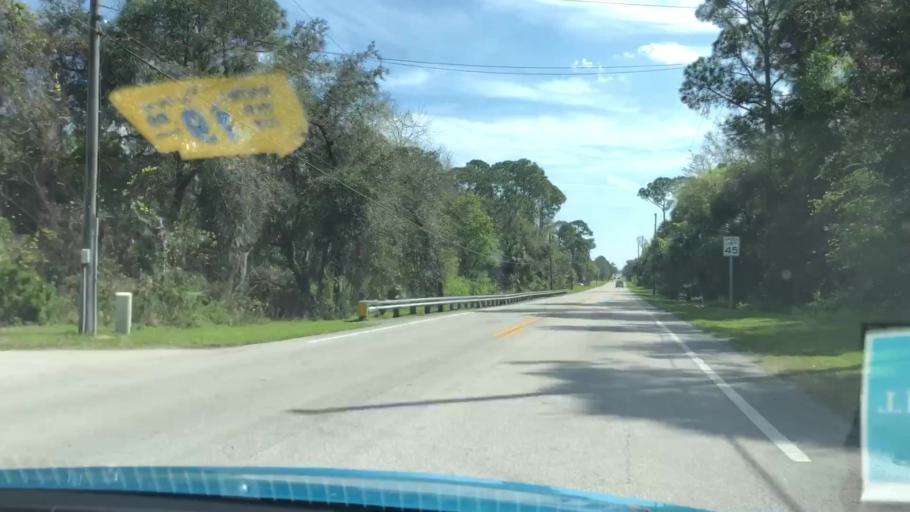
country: US
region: Florida
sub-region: Volusia County
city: Deltona
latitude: 28.8628
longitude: -81.2079
